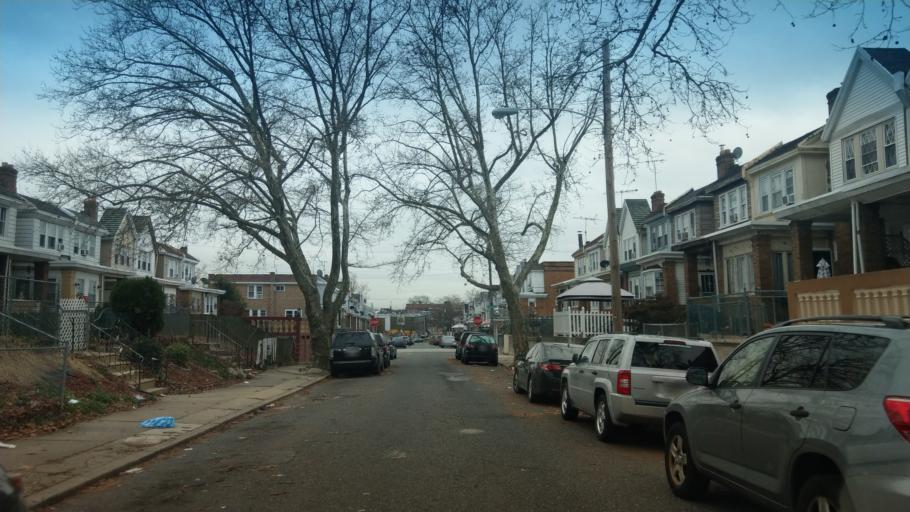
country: US
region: Pennsylvania
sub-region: Montgomery County
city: Rockledge
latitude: 40.0241
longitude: -75.1144
